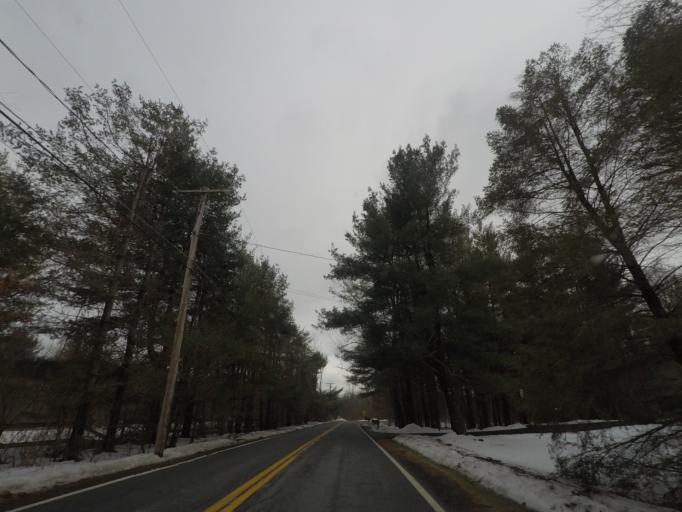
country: US
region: New York
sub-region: Schenectady County
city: Rotterdam
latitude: 42.7444
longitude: -73.9641
